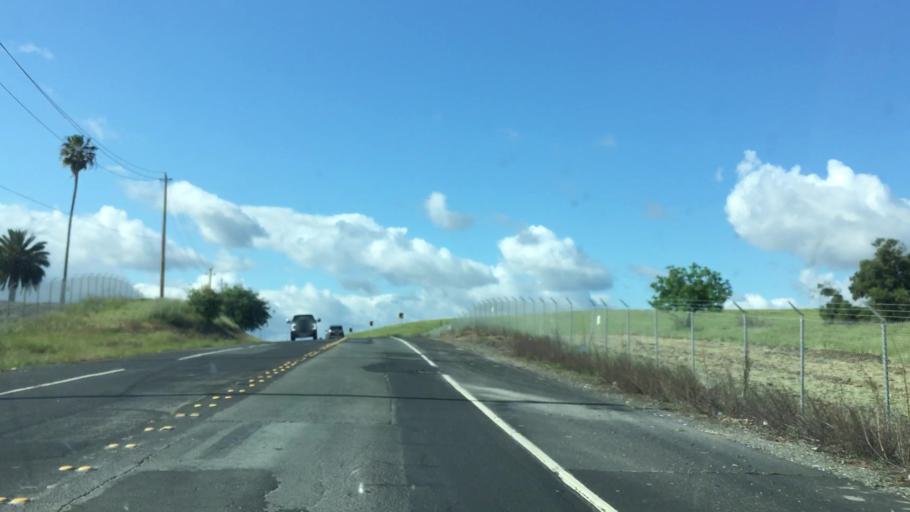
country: US
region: California
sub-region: Contra Costa County
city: Concord
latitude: 37.9979
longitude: -122.0015
